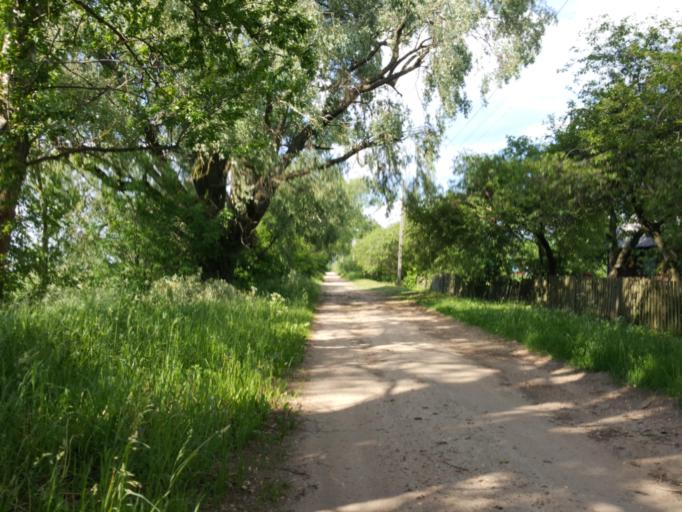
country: BY
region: Brest
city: Vysokaye
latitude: 52.4465
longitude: 23.5801
